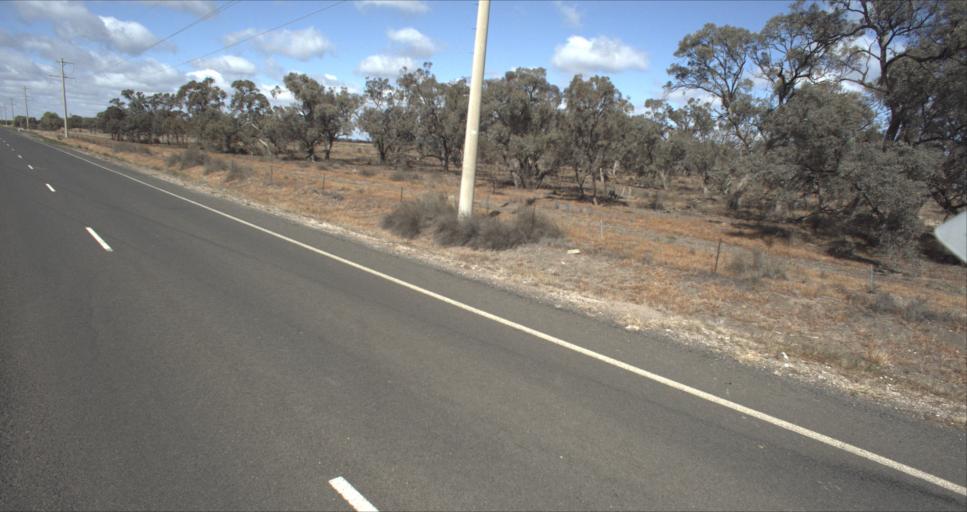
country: AU
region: New South Wales
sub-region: Murrumbidgee Shire
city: Darlington Point
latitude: -34.5242
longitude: 146.1751
